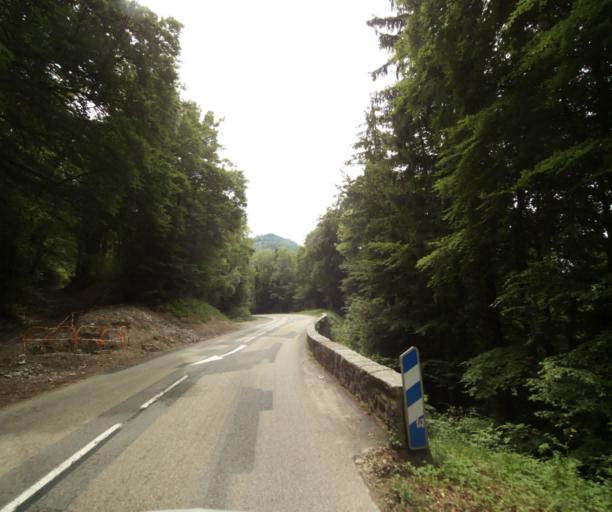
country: FR
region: Rhone-Alpes
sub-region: Departement de la Haute-Savoie
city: Perrignier
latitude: 46.2973
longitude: 6.4647
